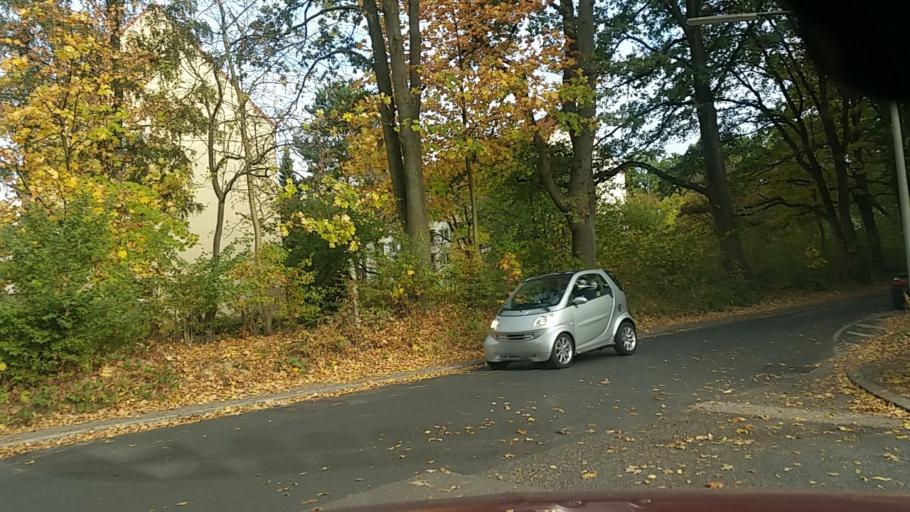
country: DE
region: Hamburg
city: Langenhorn
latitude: 53.6544
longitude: 10.0149
